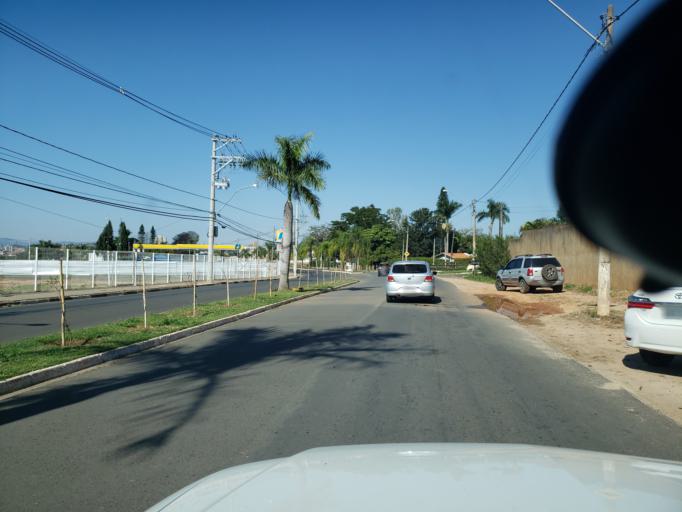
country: BR
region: Sao Paulo
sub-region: Itapira
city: Itapira
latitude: -22.4200
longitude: -46.8389
